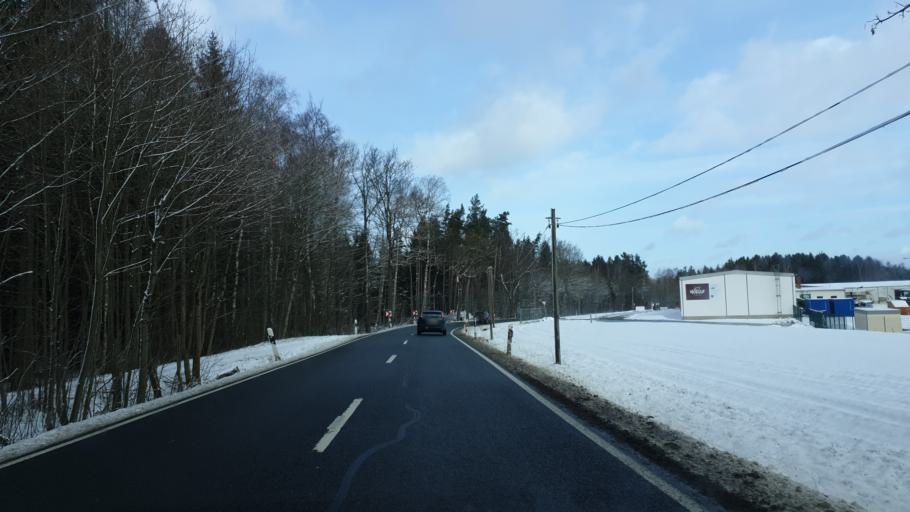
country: DE
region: Saxony
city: Eichigt
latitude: 50.3517
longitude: 12.1583
